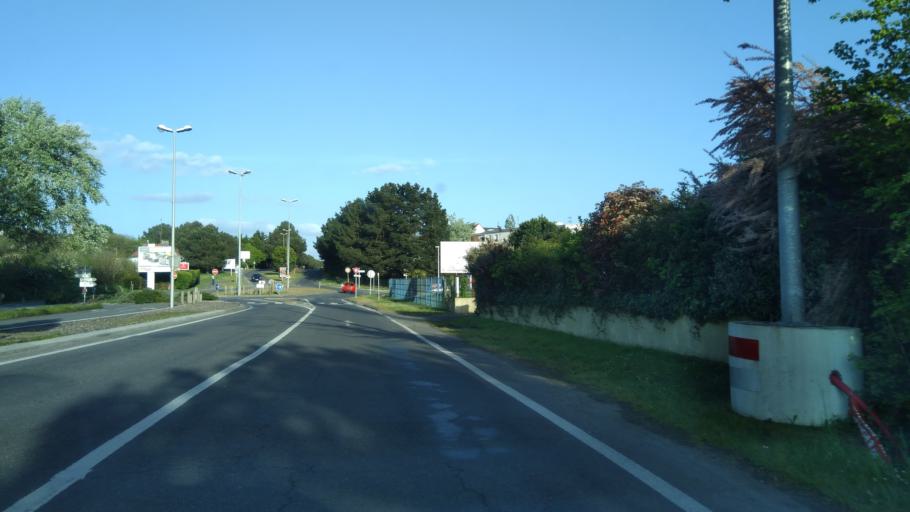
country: FR
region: Pays de la Loire
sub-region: Departement de la Loire-Atlantique
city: Pornichet
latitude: 47.2580
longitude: -2.3255
